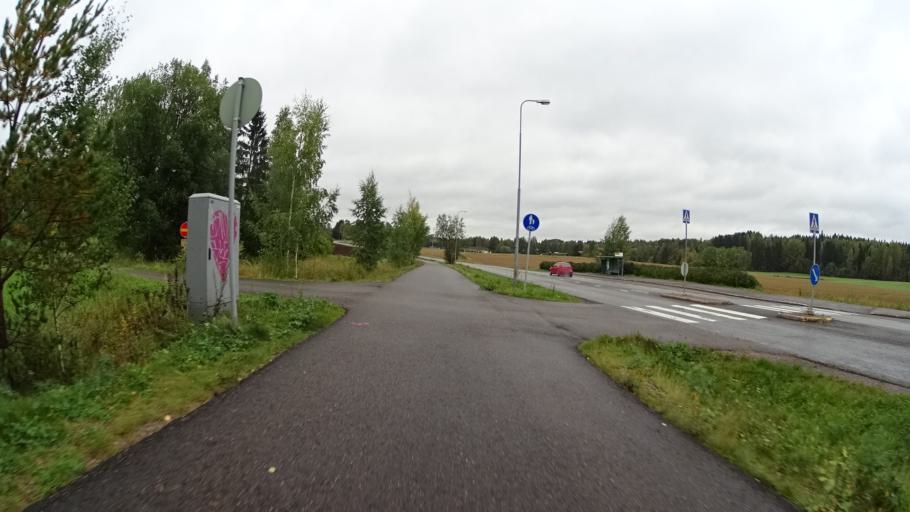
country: FI
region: Uusimaa
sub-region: Helsinki
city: Kauniainen
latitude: 60.2593
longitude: 24.7348
